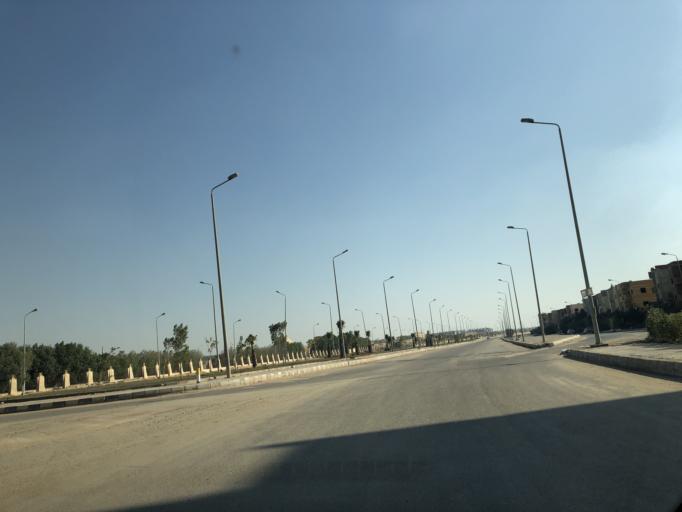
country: EG
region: Al Jizah
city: Madinat Sittah Uktubar
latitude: 29.9341
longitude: 31.0661
